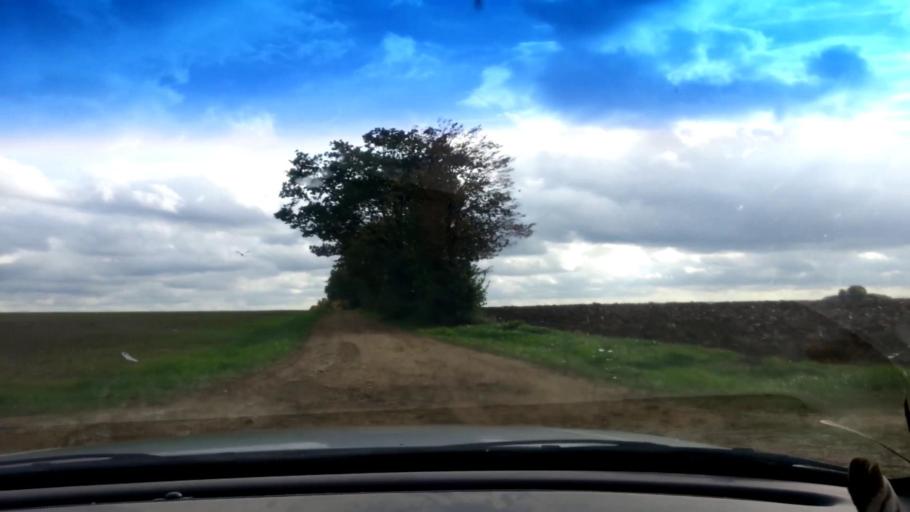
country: DE
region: Bavaria
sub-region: Upper Franconia
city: Memmelsdorf
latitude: 49.9755
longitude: 10.9658
